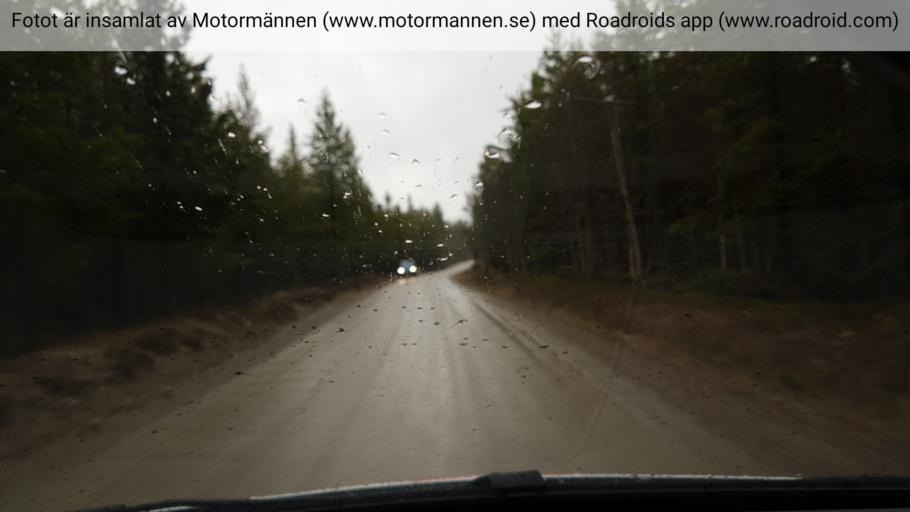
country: SE
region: Jaemtland
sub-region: Are Kommun
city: Jarpen
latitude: 62.4809
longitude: 13.5151
